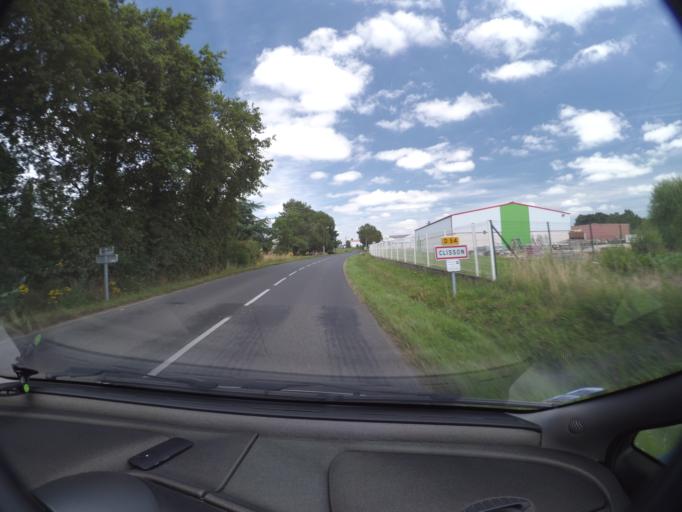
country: FR
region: Pays de la Loire
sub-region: Departement de la Loire-Atlantique
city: Clisson
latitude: 47.0772
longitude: -1.2946
